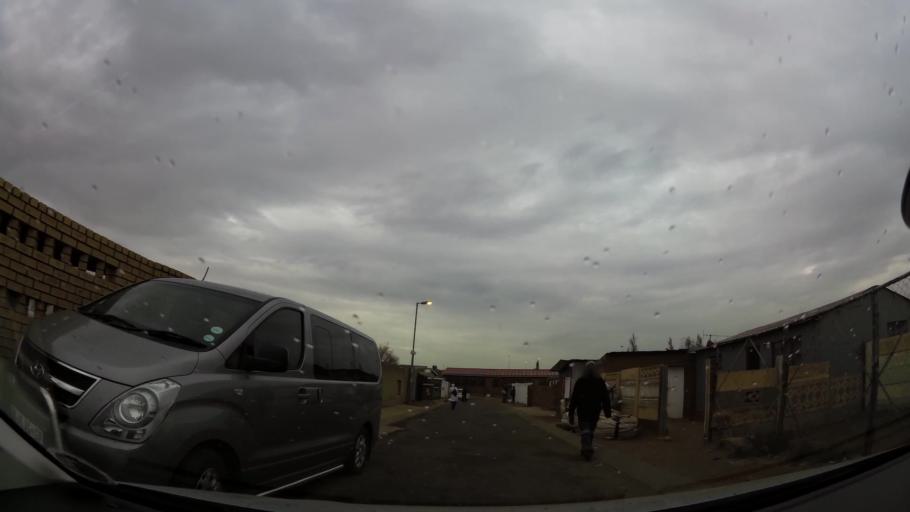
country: ZA
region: Gauteng
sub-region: City of Johannesburg Metropolitan Municipality
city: Soweto
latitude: -26.2529
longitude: 27.8651
